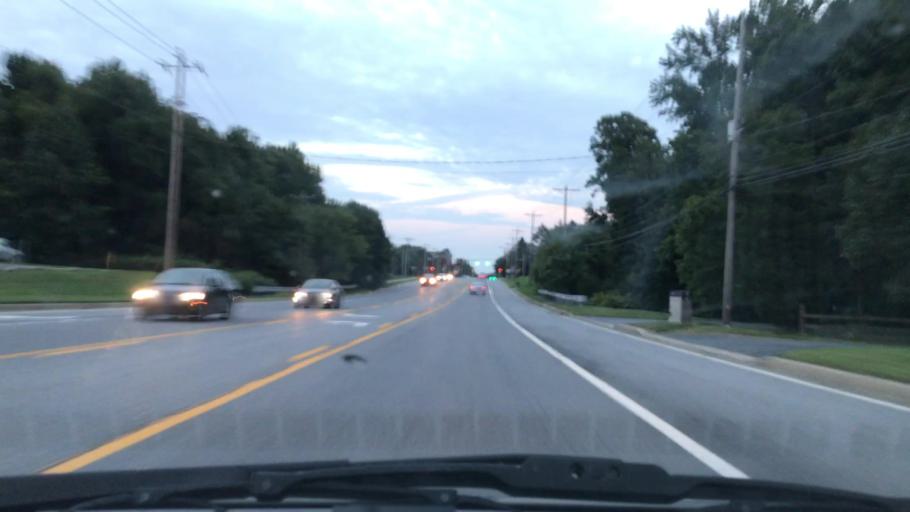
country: US
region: Delaware
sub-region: New Castle County
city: Brookside
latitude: 39.6471
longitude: -75.7112
